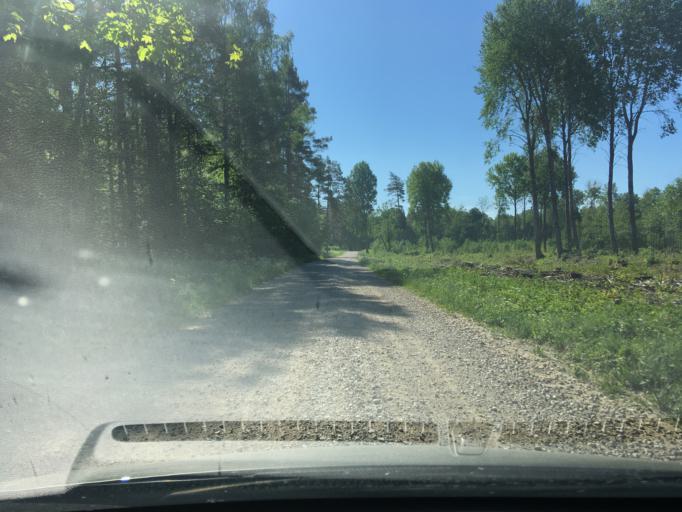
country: EE
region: Laeaene
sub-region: Lihula vald
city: Lihula
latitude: 58.6459
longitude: 23.7831
